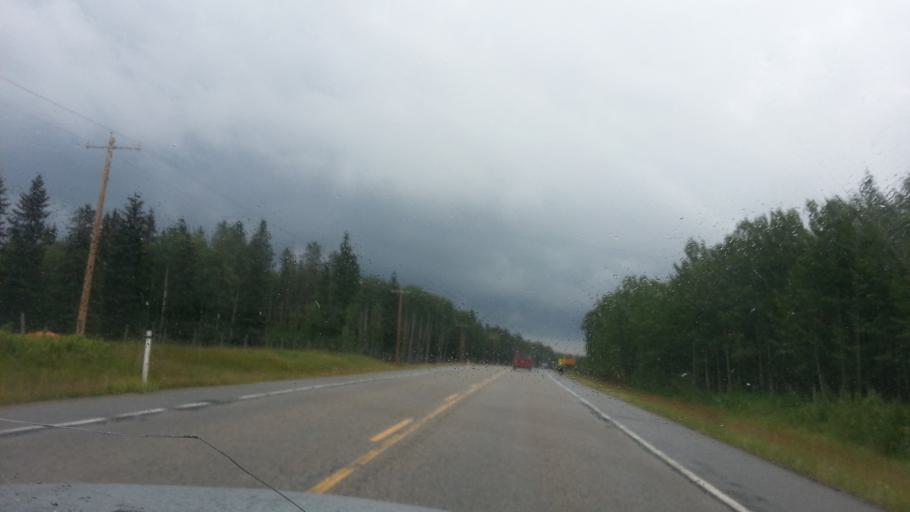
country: CA
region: Alberta
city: Cochrane
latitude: 50.9218
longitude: -114.5730
